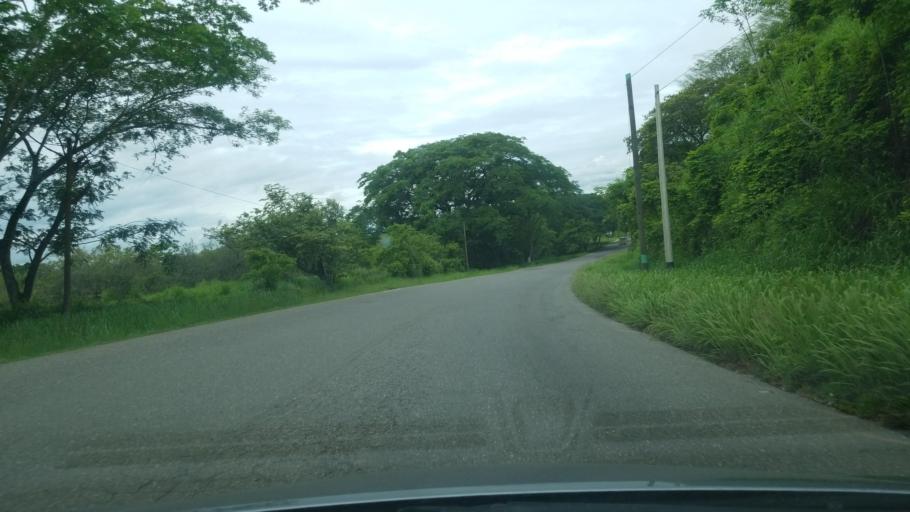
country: HN
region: Santa Barbara
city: La Flecha
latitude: 15.2959
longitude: -88.4591
